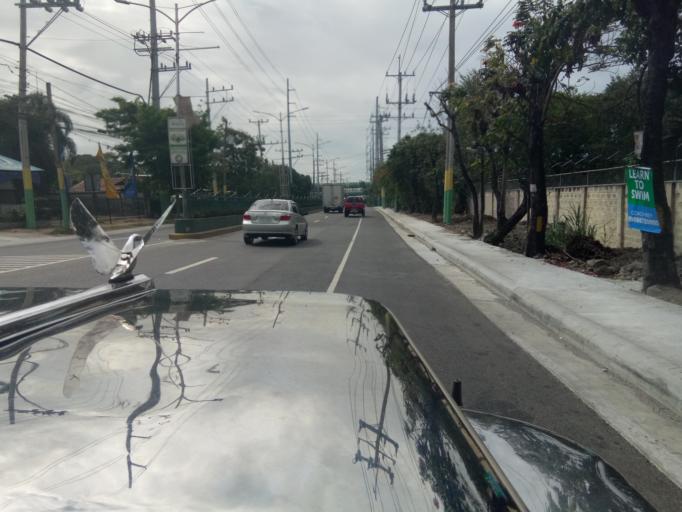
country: PH
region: Calabarzon
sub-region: Province of Cavite
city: Dasmarinas
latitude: 14.3114
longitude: 120.9489
